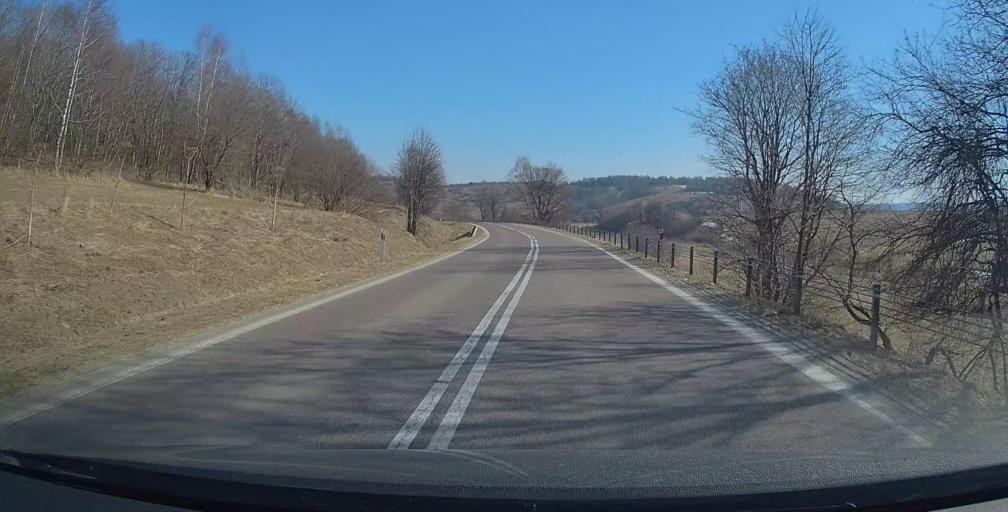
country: PL
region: Subcarpathian Voivodeship
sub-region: Powiat przemyski
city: Bircza
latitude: 49.5956
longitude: 22.4925
